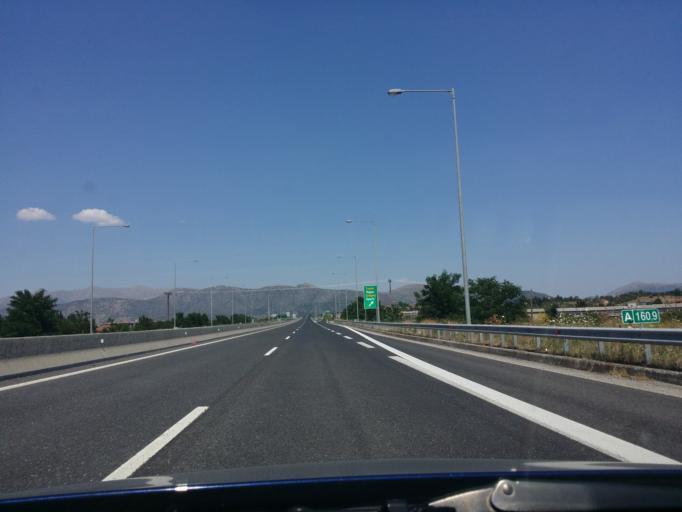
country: GR
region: Peloponnese
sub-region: Nomos Arkadias
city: Tripoli
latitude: 37.4922
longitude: 22.3746
